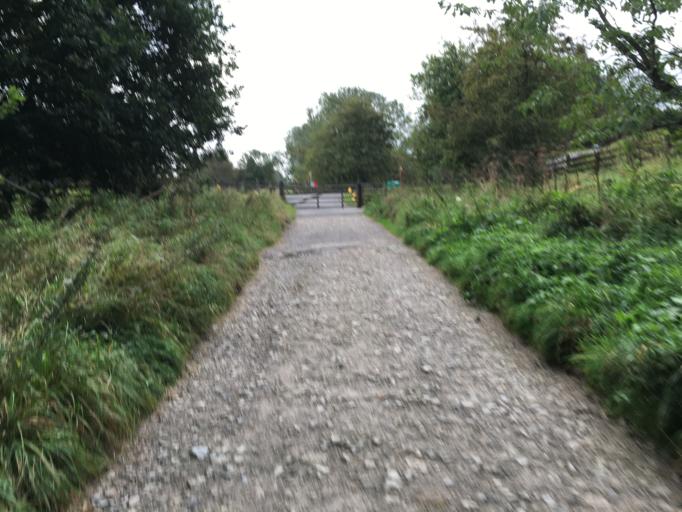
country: GB
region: England
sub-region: North Yorkshire
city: Sleights
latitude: 54.4036
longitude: -0.7226
